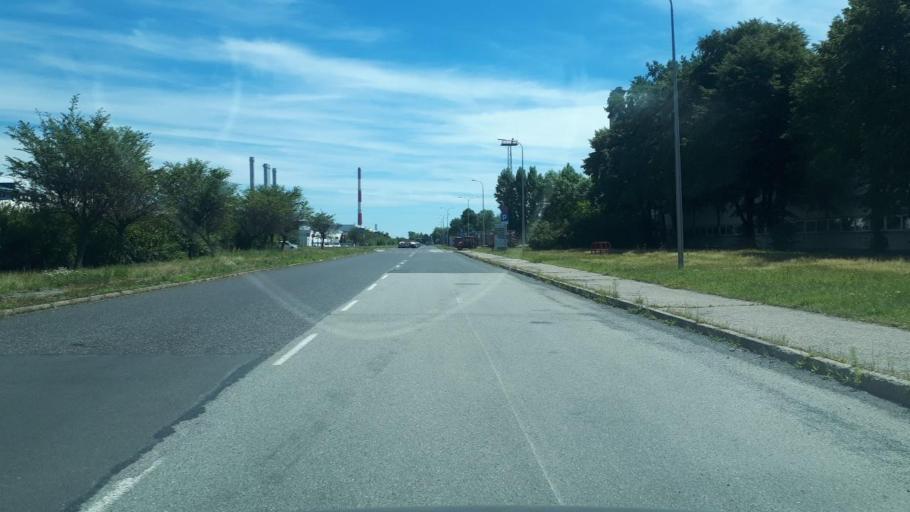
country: PL
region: Silesian Voivodeship
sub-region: Powiat bierunsko-ledzinski
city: Bierun
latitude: 50.1048
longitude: 19.0685
